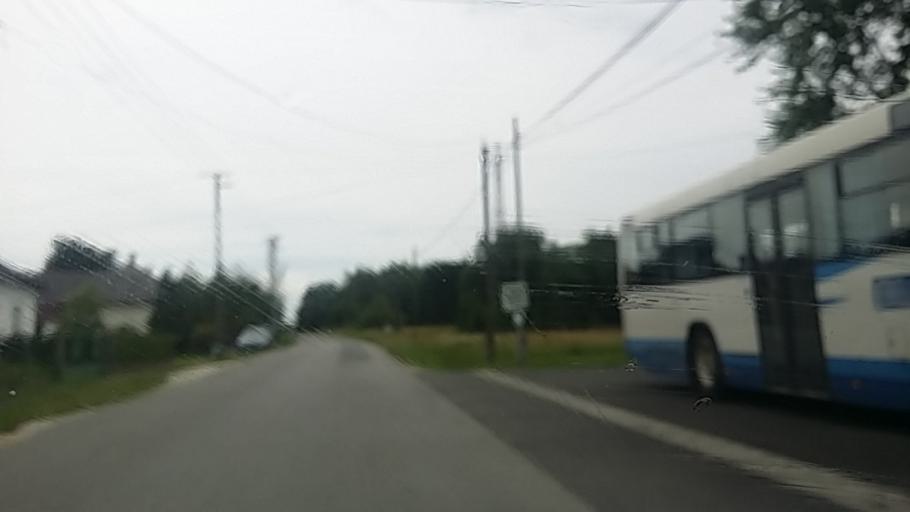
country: HU
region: Zala
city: Zalalovo
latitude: 46.8606
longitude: 16.5008
